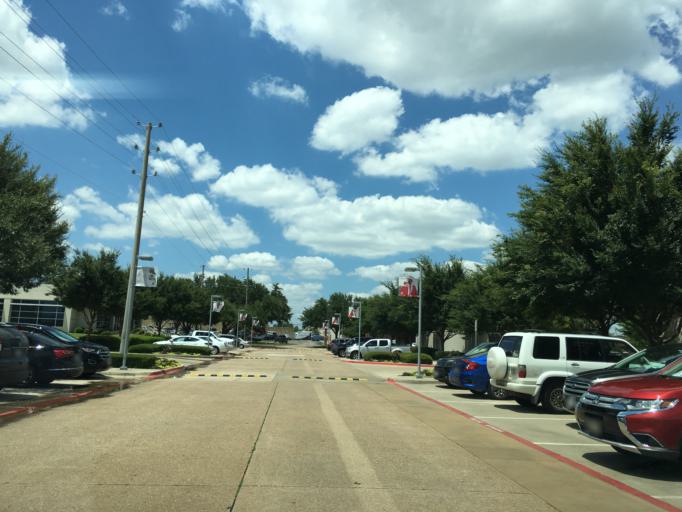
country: US
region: Texas
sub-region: Dallas County
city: Addison
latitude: 32.9492
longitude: -96.8341
